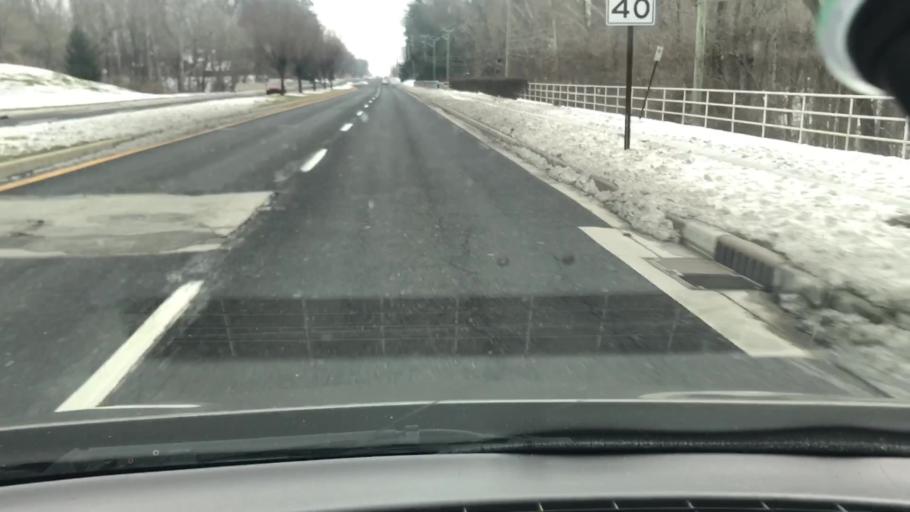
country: US
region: Indiana
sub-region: Marion County
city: Meridian Hills
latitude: 39.9123
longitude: -86.1758
